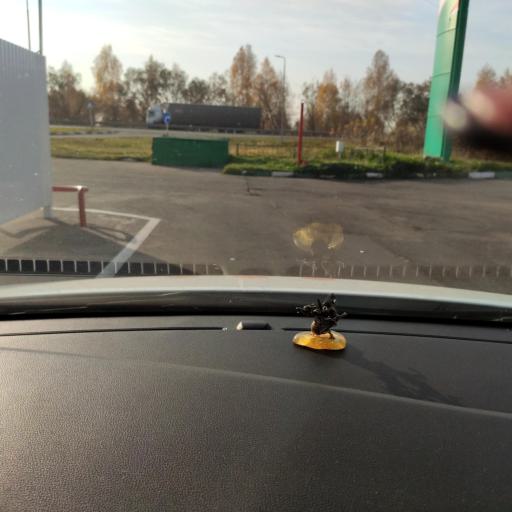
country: RU
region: Tatarstan
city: Osinovo
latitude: 55.9022
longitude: 48.9284
